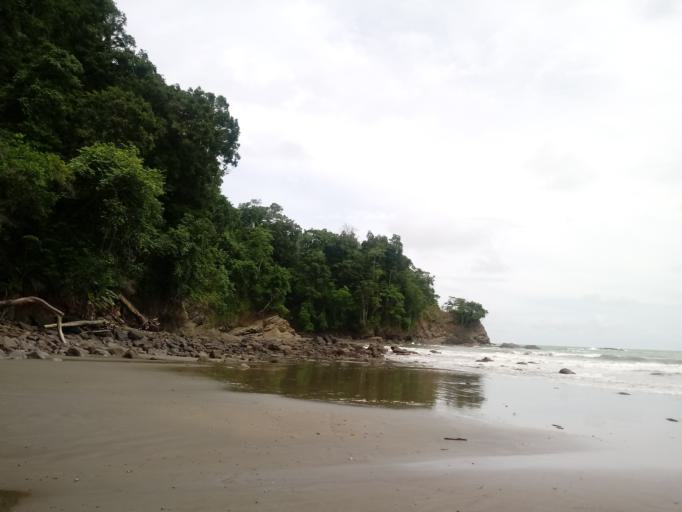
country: CR
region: San Jose
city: Mercedes
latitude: 9.0882
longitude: -83.6770
